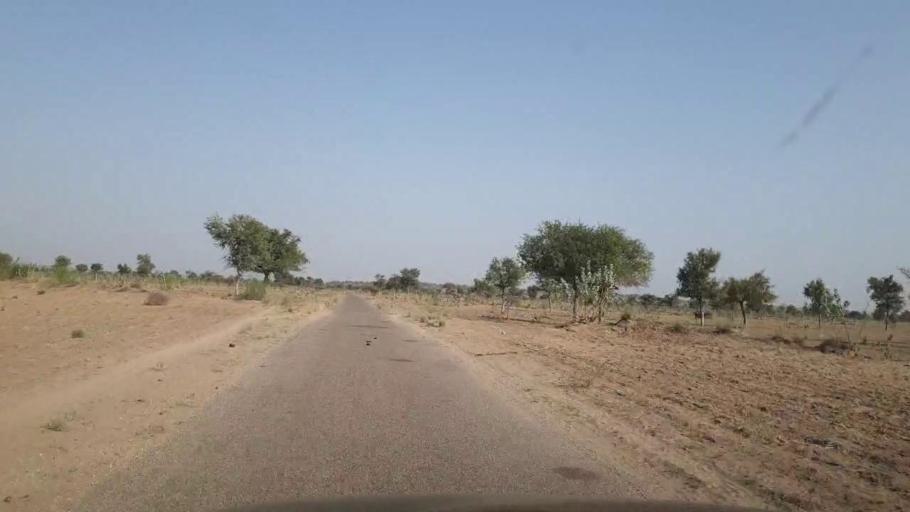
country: PK
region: Sindh
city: Islamkot
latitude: 25.1315
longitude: 70.4792
